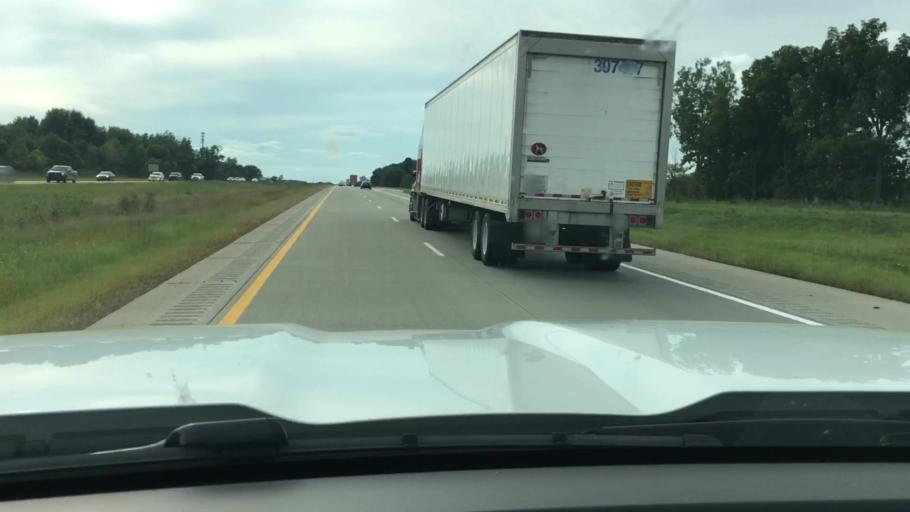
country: US
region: Michigan
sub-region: Genesee County
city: Davison
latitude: 43.0155
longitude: -83.4423
